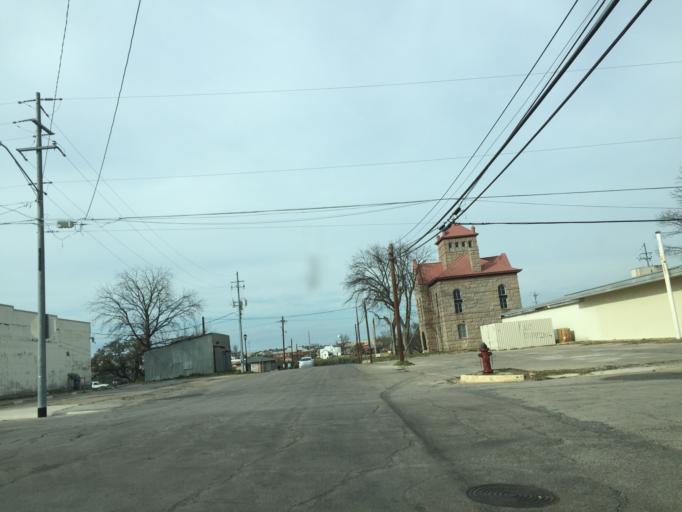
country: US
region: Texas
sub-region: Llano County
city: Llano
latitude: 30.7502
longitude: -98.6748
